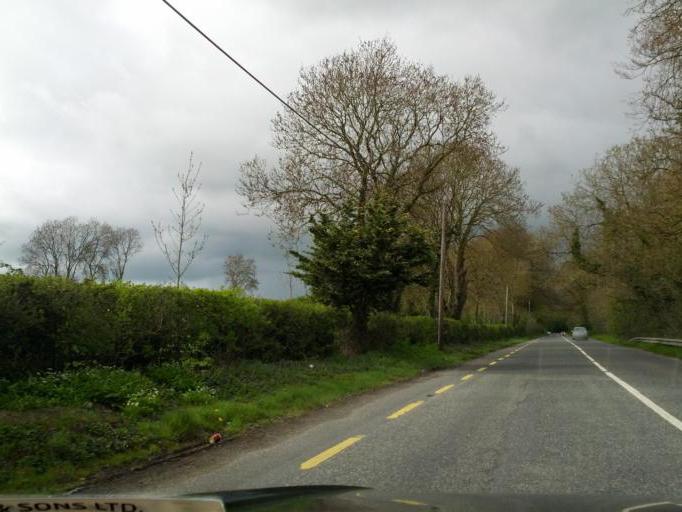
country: IE
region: Leinster
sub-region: An Mhi
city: Dunshaughlin
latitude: 53.5267
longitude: -6.5566
